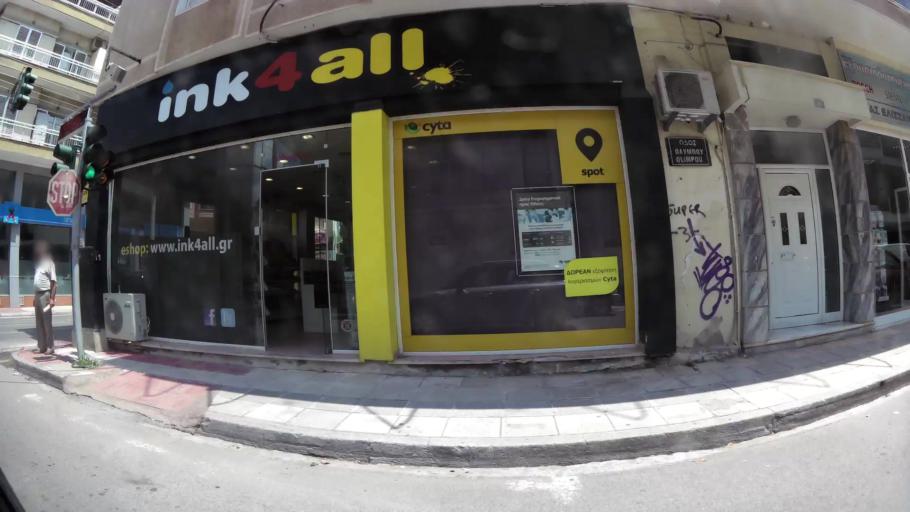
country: GR
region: West Macedonia
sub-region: Nomos Kozanis
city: Kozani
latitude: 40.2971
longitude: 21.7920
